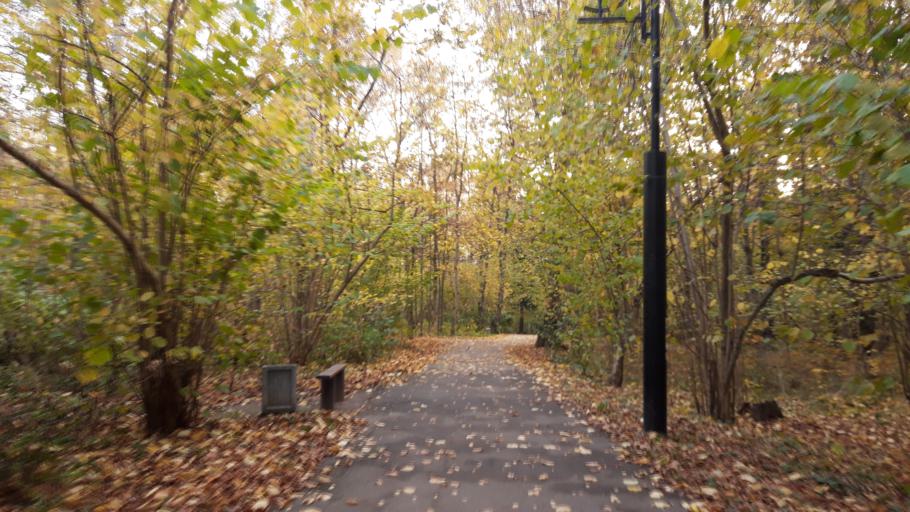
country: RU
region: Moscow
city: Zelenograd
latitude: 55.9979
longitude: 37.1973
